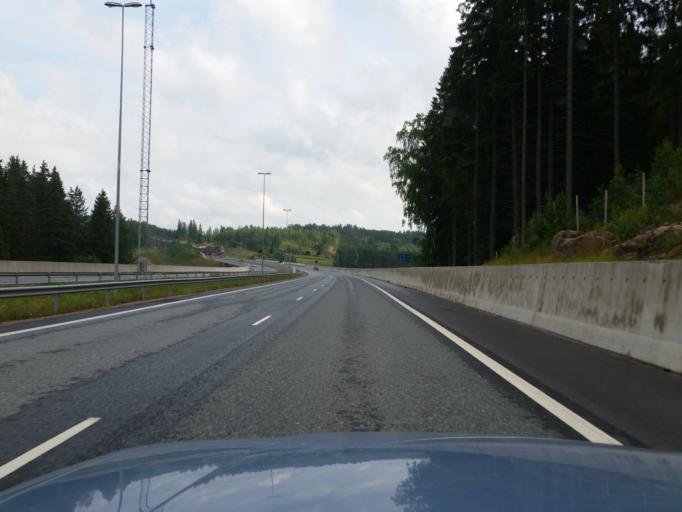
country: FI
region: Uusimaa
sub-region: Helsinki
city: Saukkola
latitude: 60.3335
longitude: 23.9295
